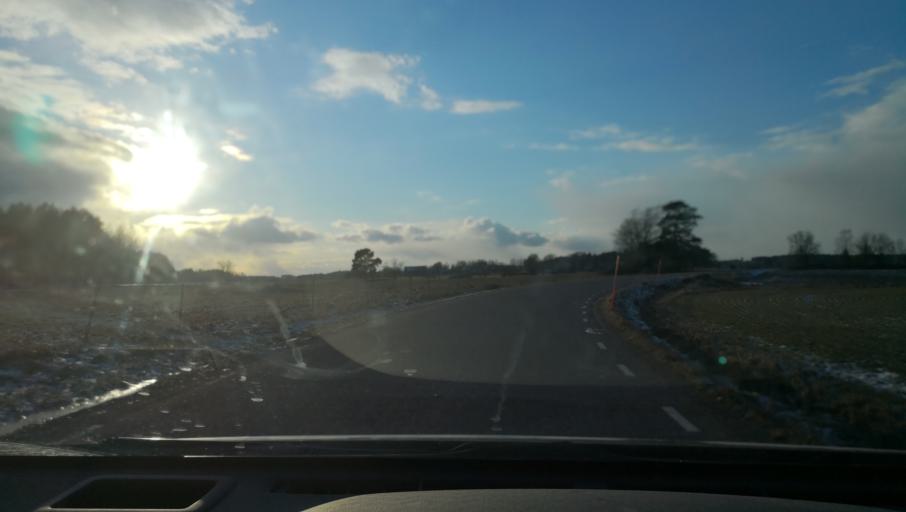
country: SE
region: Vaestmanland
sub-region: Vasteras
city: Tillberga
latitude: 59.6385
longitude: 16.7183
